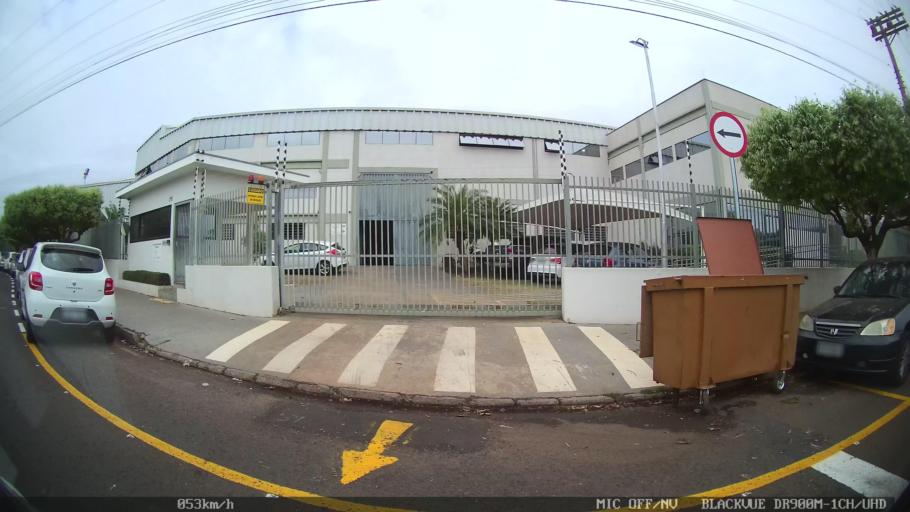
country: BR
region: Sao Paulo
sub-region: Sao Jose Do Rio Preto
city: Sao Jose do Rio Preto
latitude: -20.8276
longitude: -49.4200
